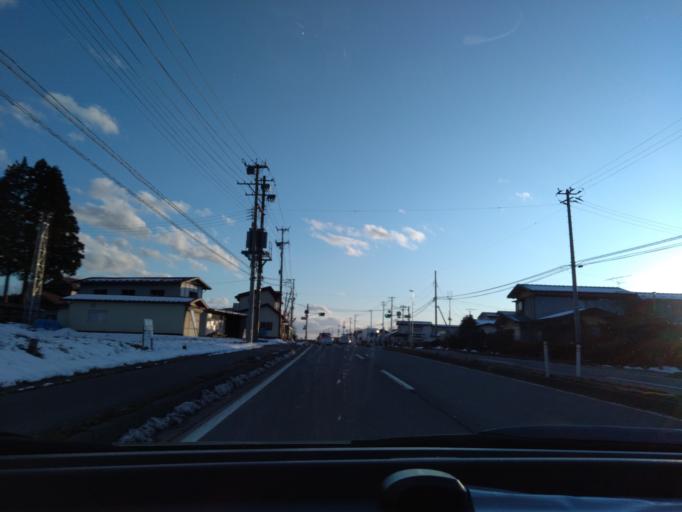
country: JP
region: Iwate
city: Hanamaki
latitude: 39.5278
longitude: 141.1632
